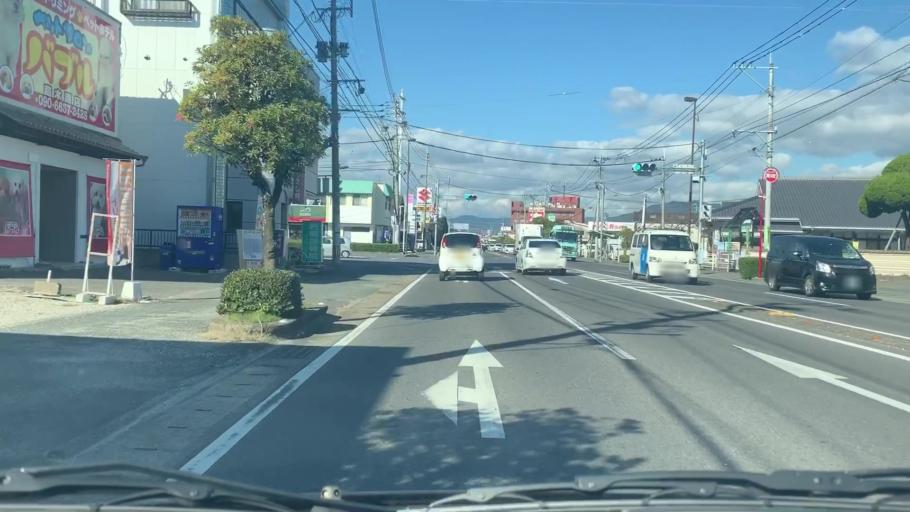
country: JP
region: Saga Prefecture
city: Saga-shi
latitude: 33.2858
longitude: 130.2901
